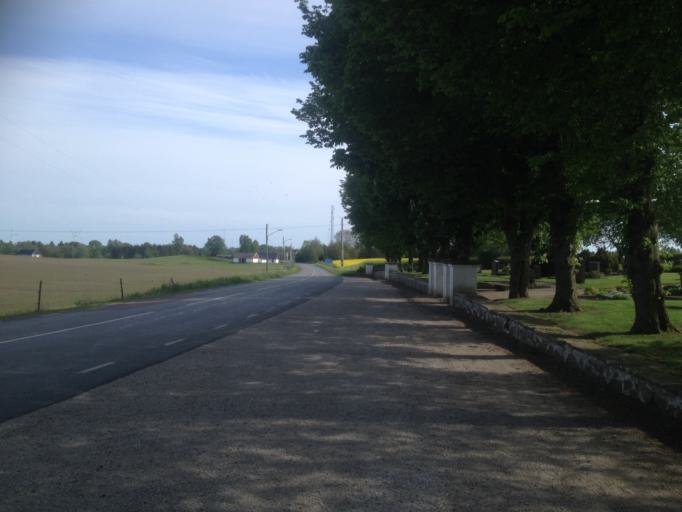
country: SE
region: Skane
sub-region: Tomelilla Kommun
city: Tomelilla
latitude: 55.5618
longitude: 14.1110
